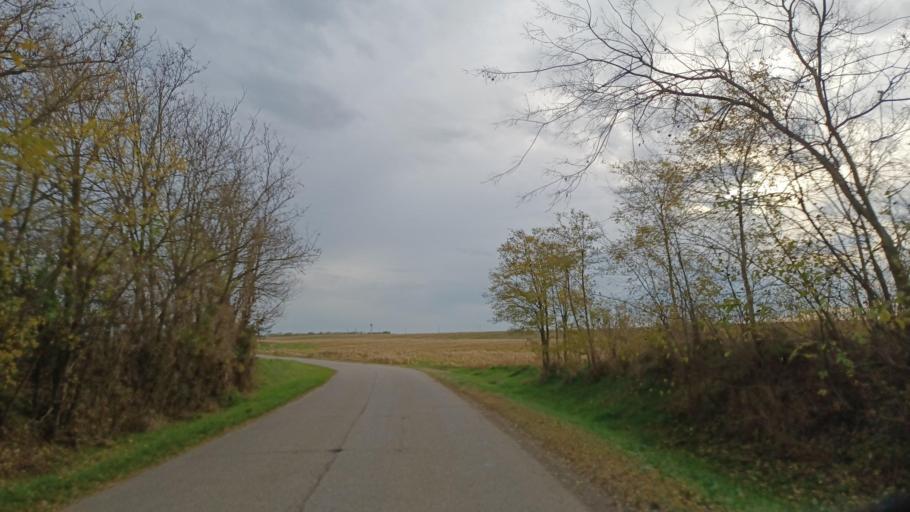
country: HU
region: Tolna
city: Nagydorog
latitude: 46.6479
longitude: 18.6077
